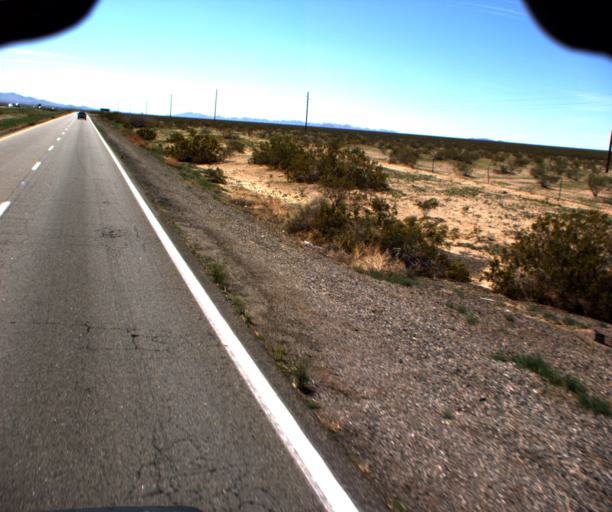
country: US
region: Arizona
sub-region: Mohave County
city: Dolan Springs
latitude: 35.6200
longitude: -114.4191
